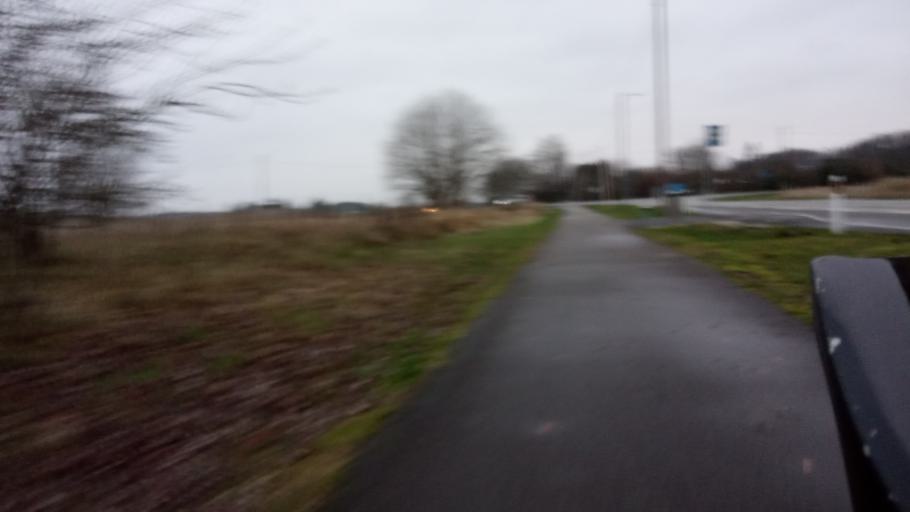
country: EE
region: Harju
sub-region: Kuusalu vald
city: Kuusalu
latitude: 59.4525
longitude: 25.4332
